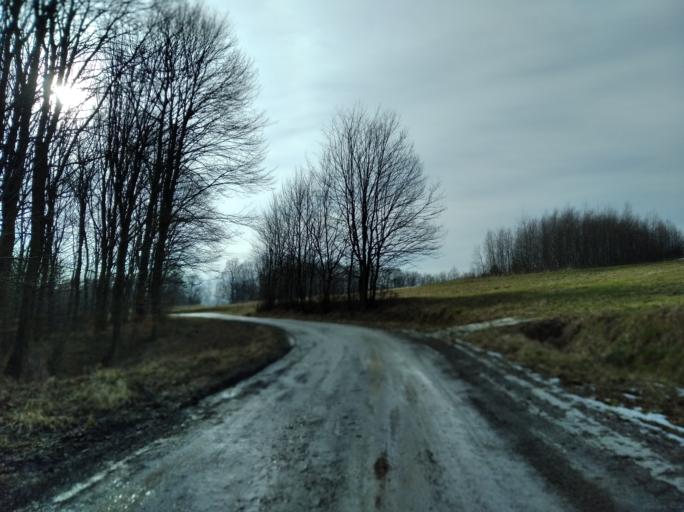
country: PL
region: Subcarpathian Voivodeship
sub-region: Powiat brzozowski
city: Gorki
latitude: 49.6411
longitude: 22.0624
